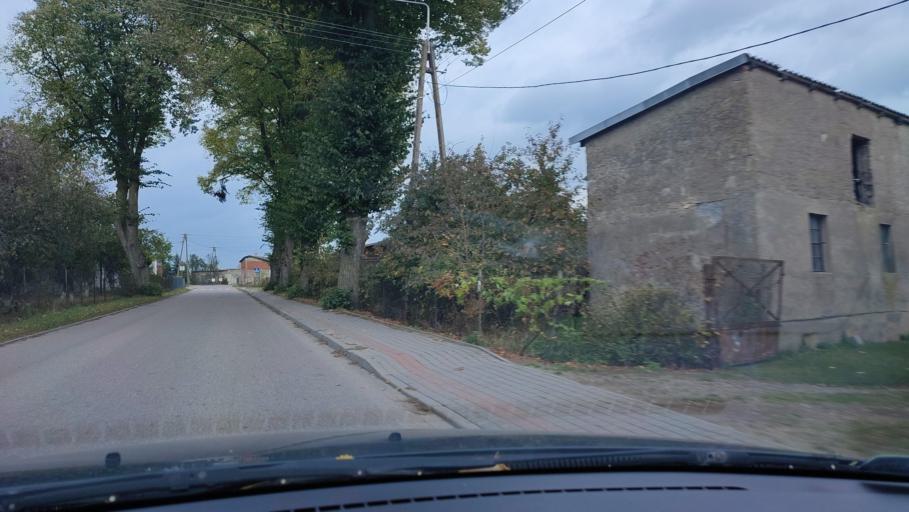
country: PL
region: Masovian Voivodeship
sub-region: Powiat mlawski
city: Wieczfnia Koscielna
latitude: 53.2121
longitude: 20.3947
